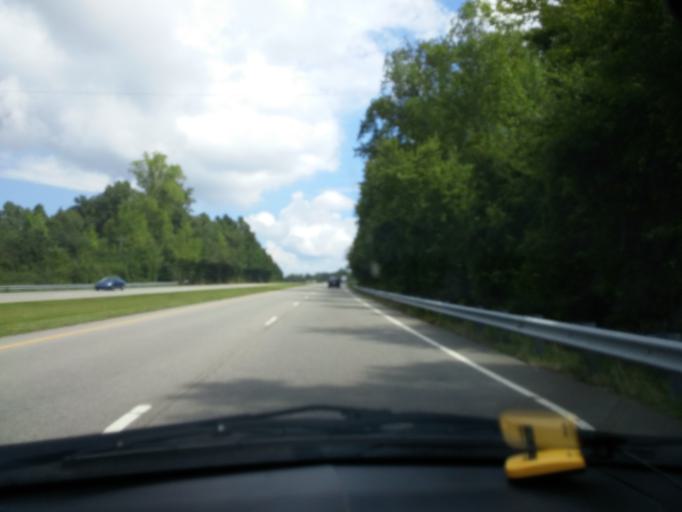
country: US
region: North Carolina
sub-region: Lenoir County
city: Kinston
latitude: 35.3087
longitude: -77.5236
